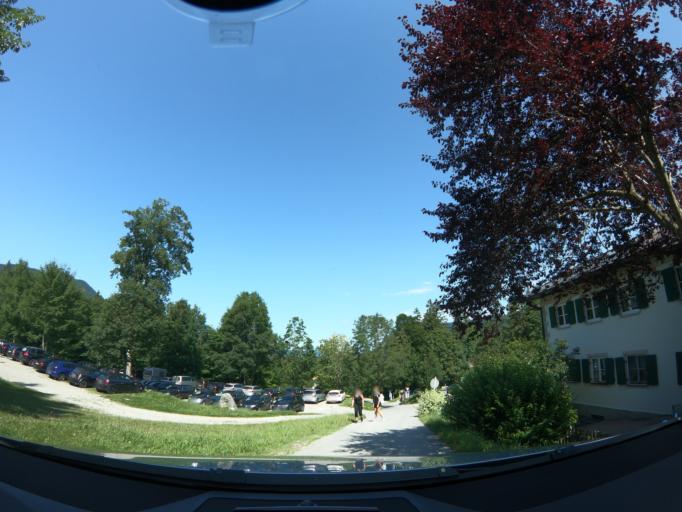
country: DE
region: Bavaria
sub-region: Upper Bavaria
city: Rottach-Egern
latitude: 47.6748
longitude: 11.7763
